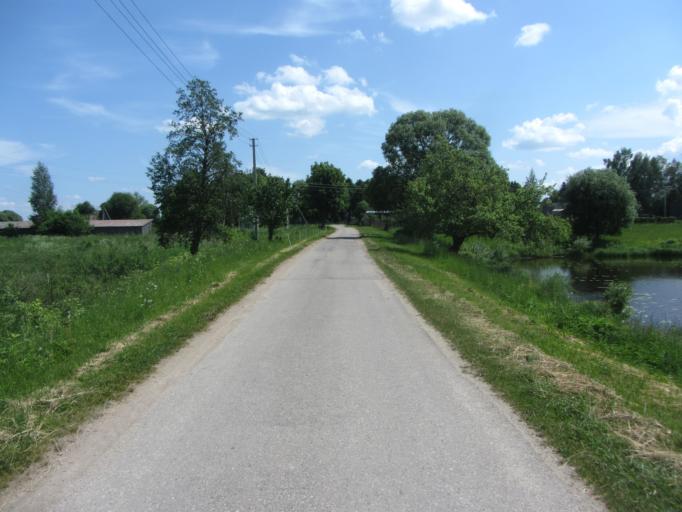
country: LT
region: Vilnius County
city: Elektrenai
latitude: 54.8879
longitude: 24.5913
